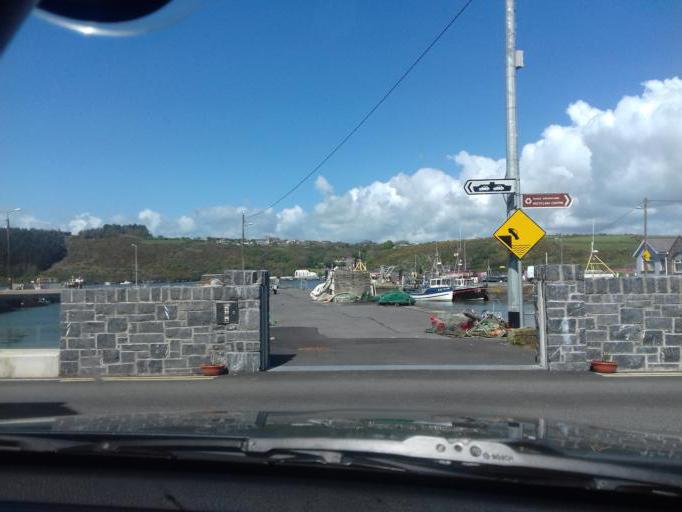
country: IE
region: Munster
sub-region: Waterford
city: Dunmore East
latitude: 52.2394
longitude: -6.9728
